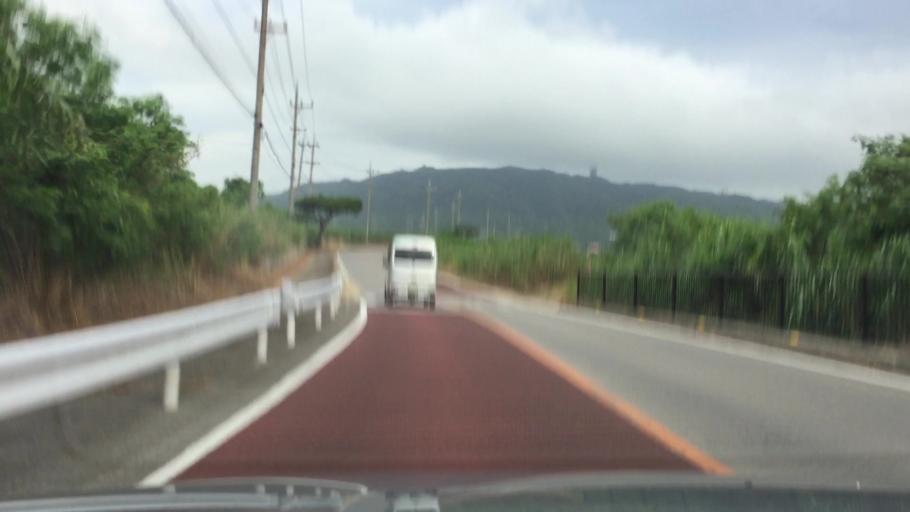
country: JP
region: Okinawa
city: Ishigaki
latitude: 24.4007
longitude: 124.1503
